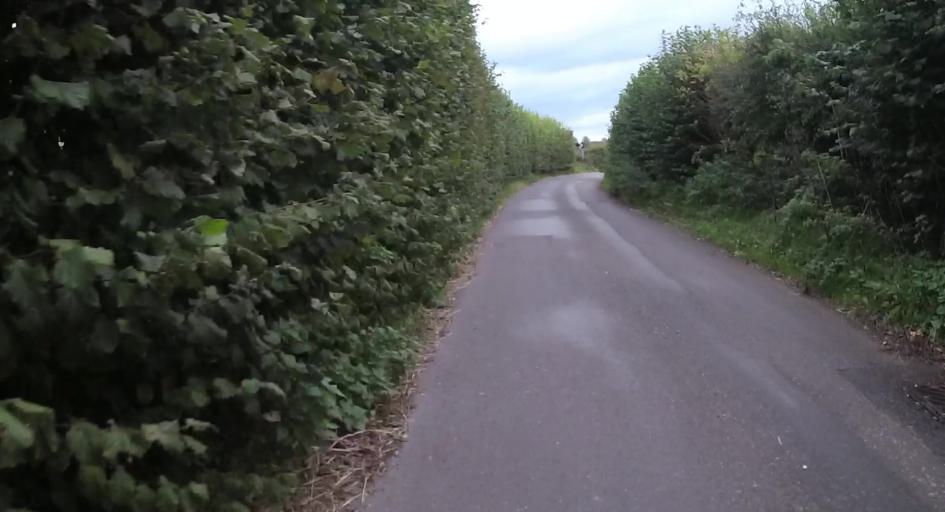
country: GB
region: England
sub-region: Hampshire
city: Alton
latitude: 51.1107
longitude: -0.9997
